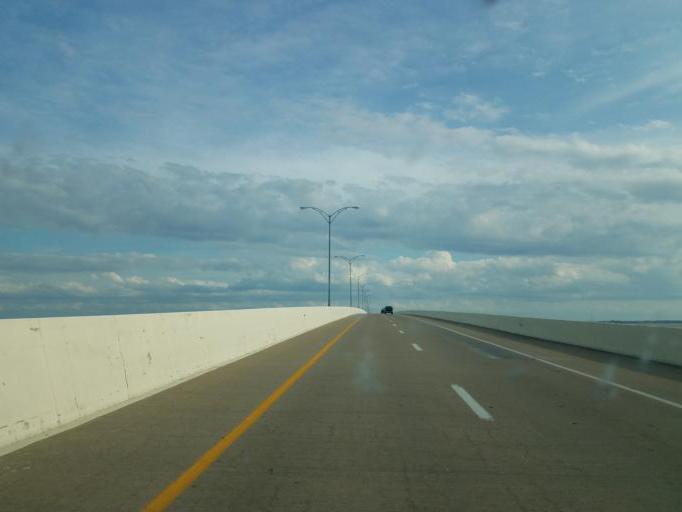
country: US
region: Ohio
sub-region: Ottawa County
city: Port Clinton
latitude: 41.4838
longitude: -82.8349
